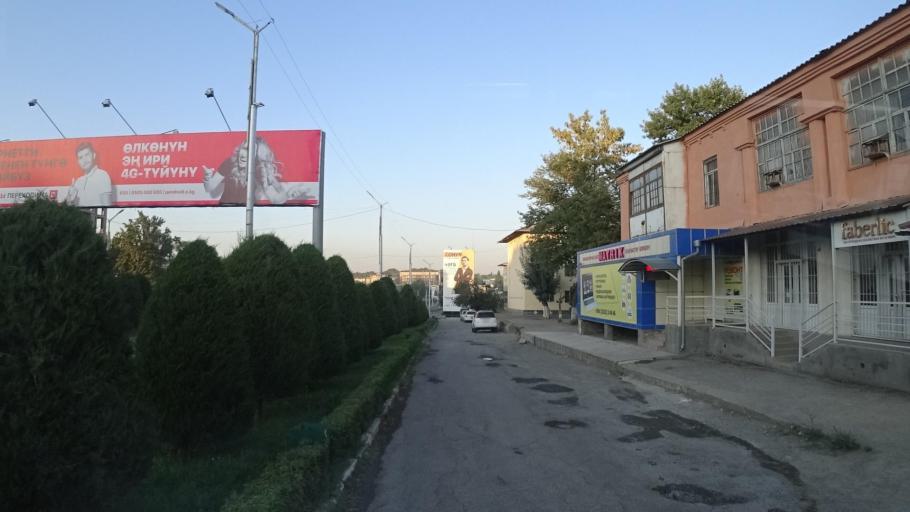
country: KG
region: Osh
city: Osh
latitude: 40.5252
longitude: 72.7988
